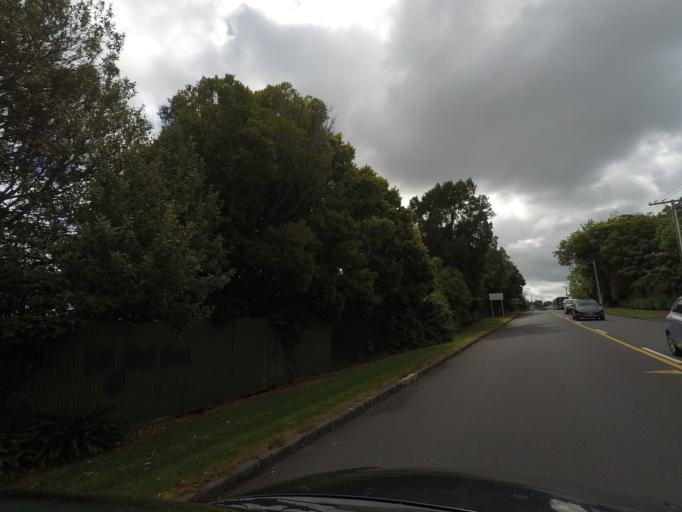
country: NZ
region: Auckland
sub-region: Auckland
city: Auckland
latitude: -36.8881
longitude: 174.8105
